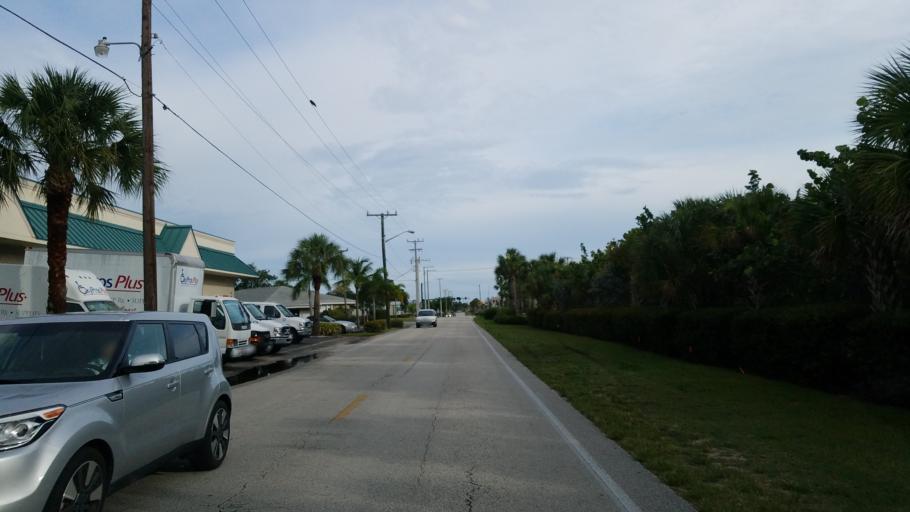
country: US
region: Florida
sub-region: Martin County
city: Stuart
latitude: 27.1922
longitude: -80.2477
